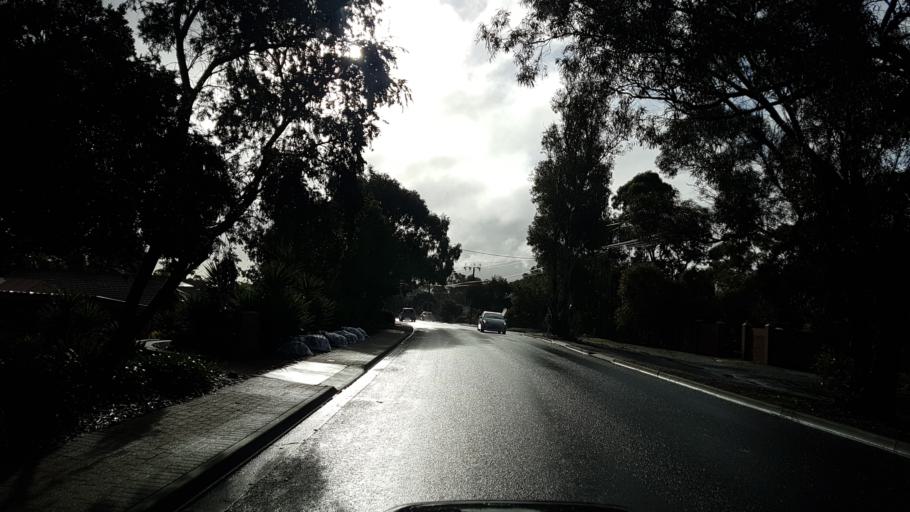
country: AU
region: South Australia
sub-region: Onkaparinga
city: Craigburn Farm
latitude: -35.0606
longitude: 138.6049
